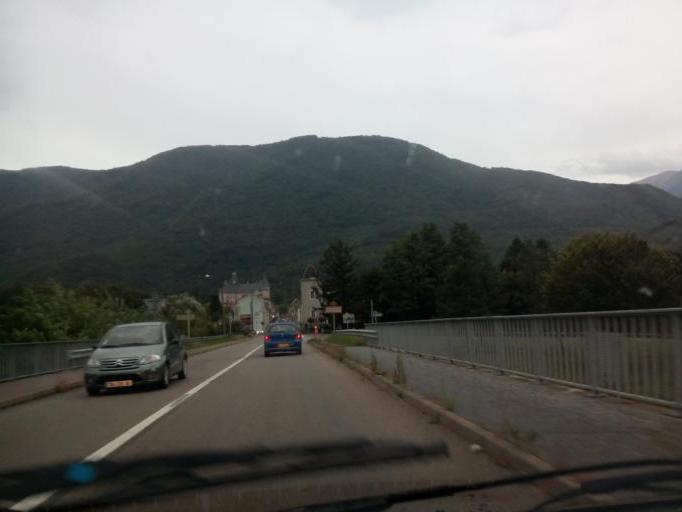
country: FR
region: Rhone-Alpes
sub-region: Departement de l'Isere
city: Vizille
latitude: 45.0735
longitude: 5.7666
